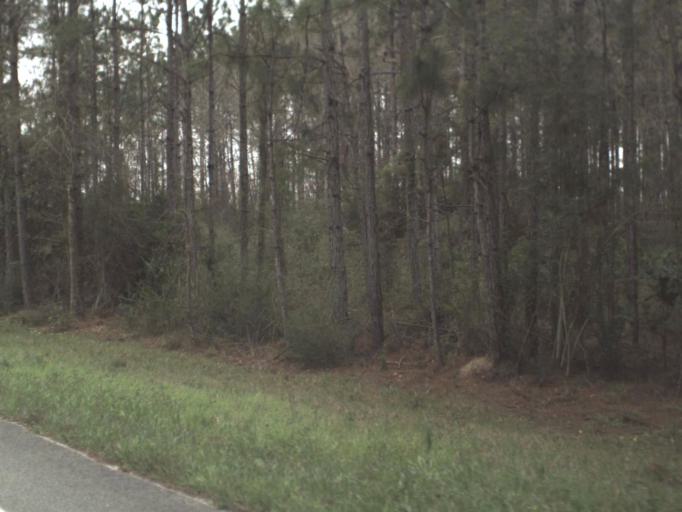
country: US
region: Florida
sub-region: Gulf County
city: Port Saint Joe
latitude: 29.9354
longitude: -85.1905
